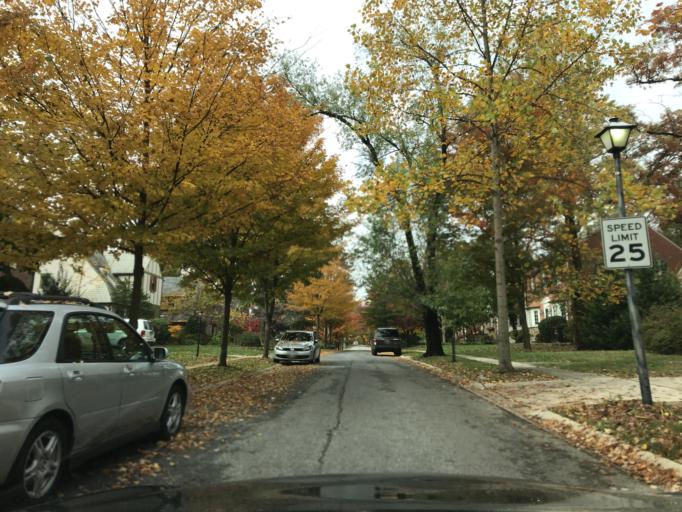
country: US
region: Maryland
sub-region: Baltimore County
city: Towson
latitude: 39.3786
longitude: -76.5983
